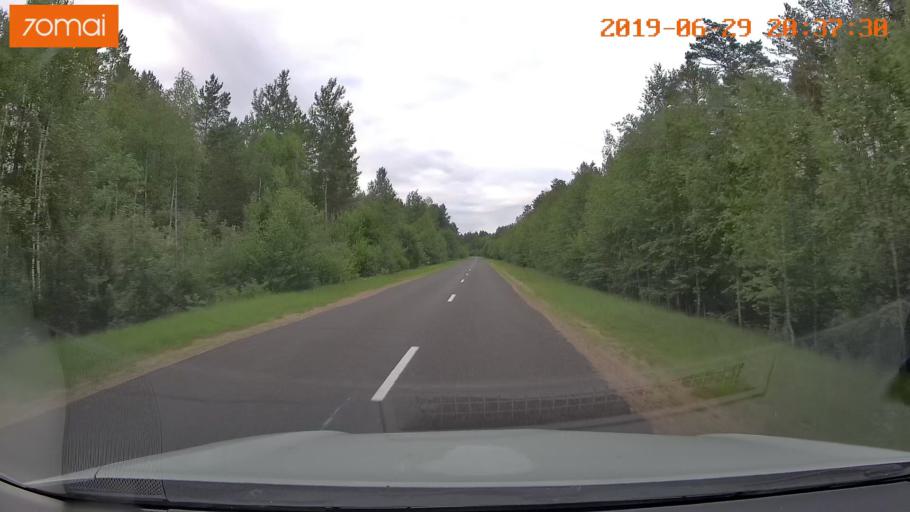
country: BY
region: Brest
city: Hantsavichy
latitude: 52.5388
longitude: 26.3647
